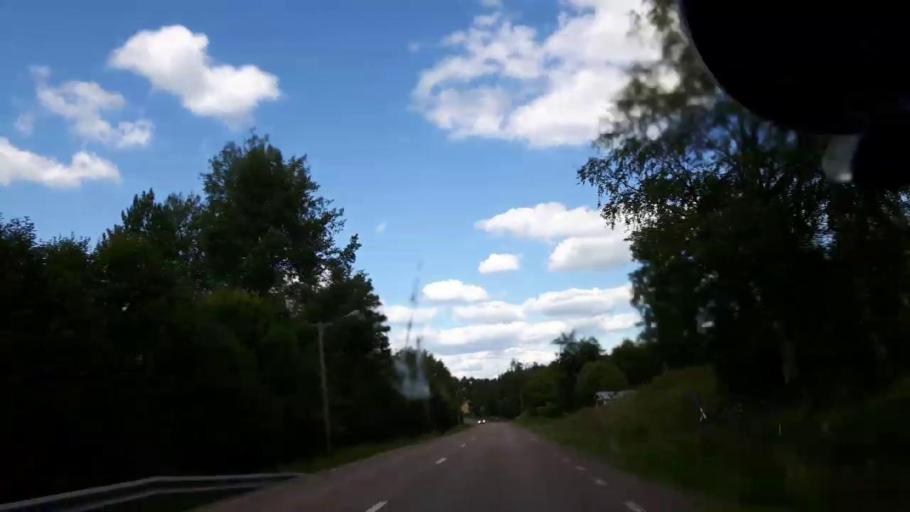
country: SE
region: Jaemtland
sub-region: Ragunda Kommun
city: Hammarstrand
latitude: 62.9955
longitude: 16.6770
